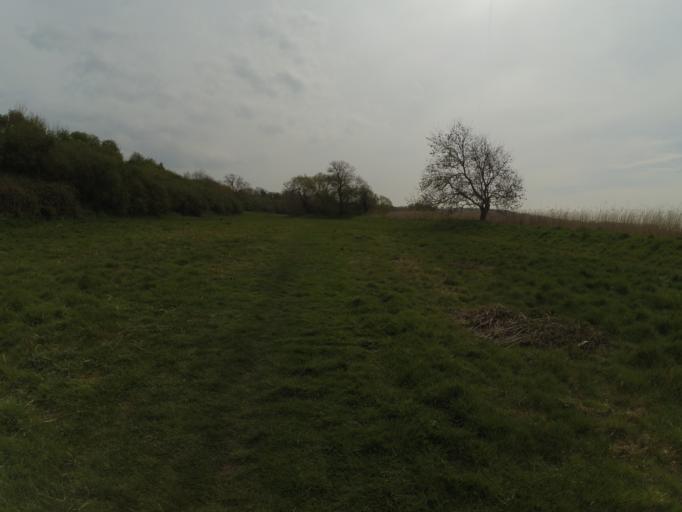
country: GB
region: England
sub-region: West Sussex
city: Arundel
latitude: 50.8722
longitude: -0.5297
